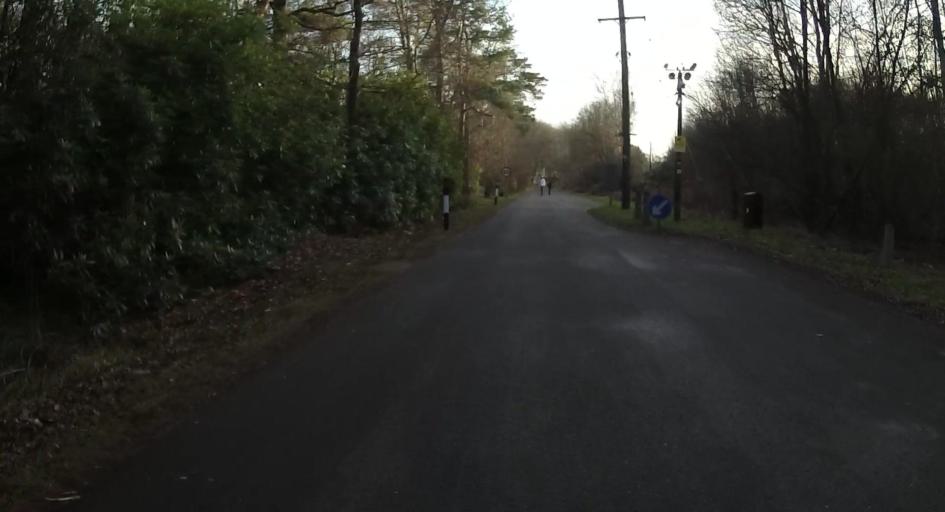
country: GB
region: England
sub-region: Bracknell Forest
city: Crowthorne
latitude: 51.3792
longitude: -0.8141
